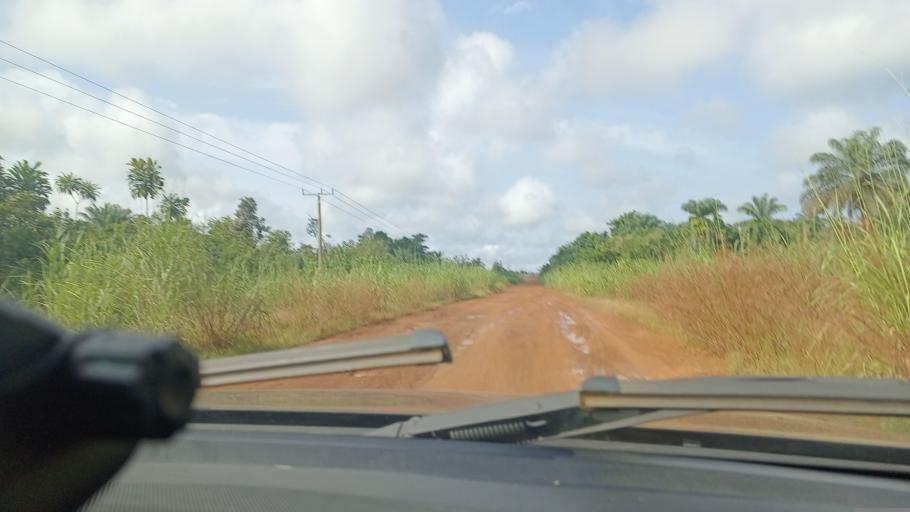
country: LR
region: Grand Cape Mount
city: Robertsport
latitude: 6.7002
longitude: -11.0948
